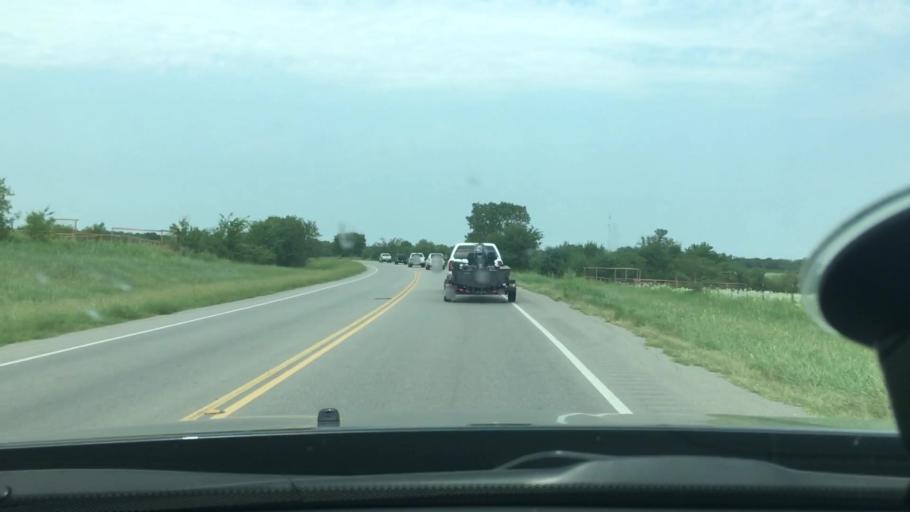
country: US
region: Oklahoma
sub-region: Marshall County
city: Madill
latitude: 34.0605
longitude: -96.7516
